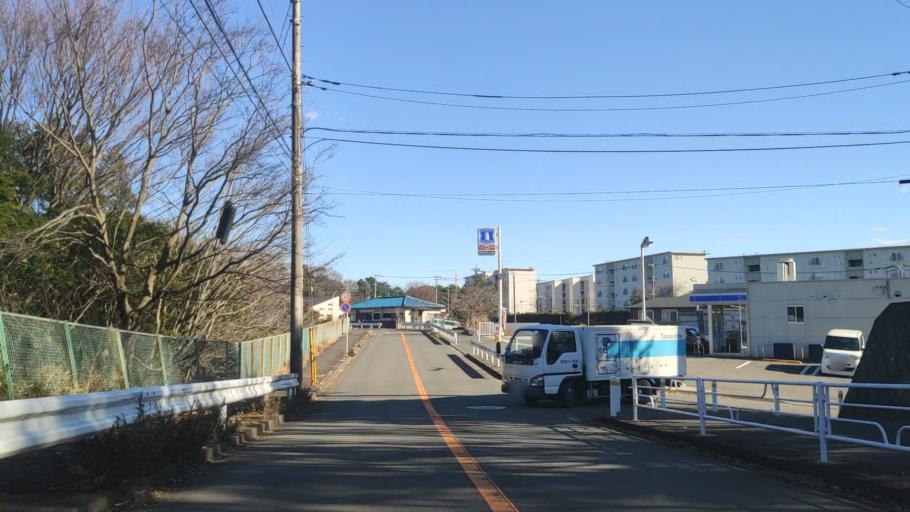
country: JP
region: Kanagawa
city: Minami-rinkan
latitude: 35.5034
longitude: 139.5284
